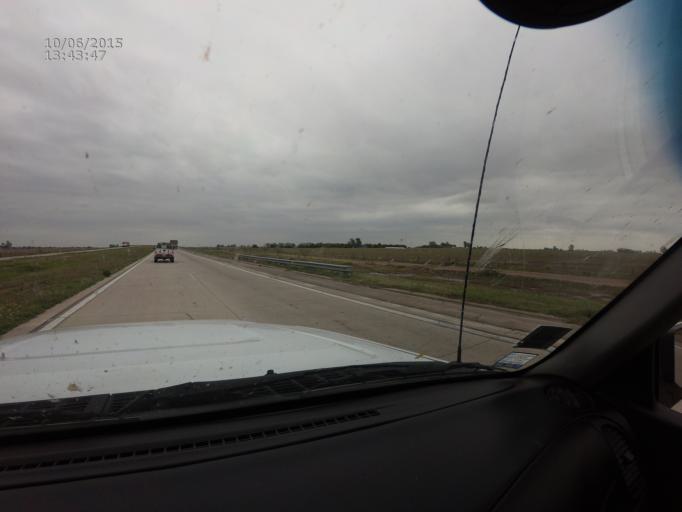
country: AR
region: Cordoba
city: Bell Ville
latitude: -32.5839
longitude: -62.5495
